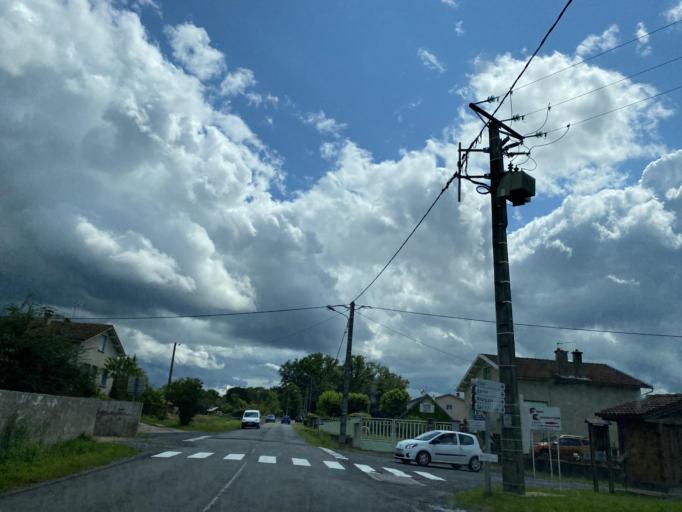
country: FR
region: Auvergne
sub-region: Departement du Puy-de-Dome
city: Peschadoires
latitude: 45.8269
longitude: 3.4868
